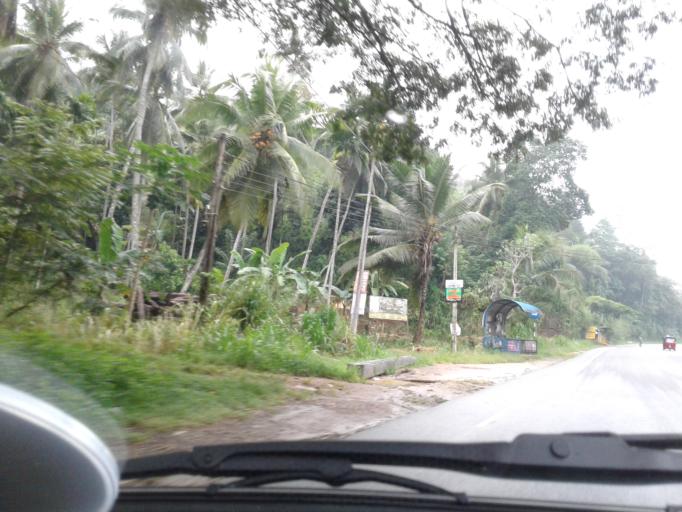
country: LK
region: Central
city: Kadugannawa
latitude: 7.2335
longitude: 80.2543
